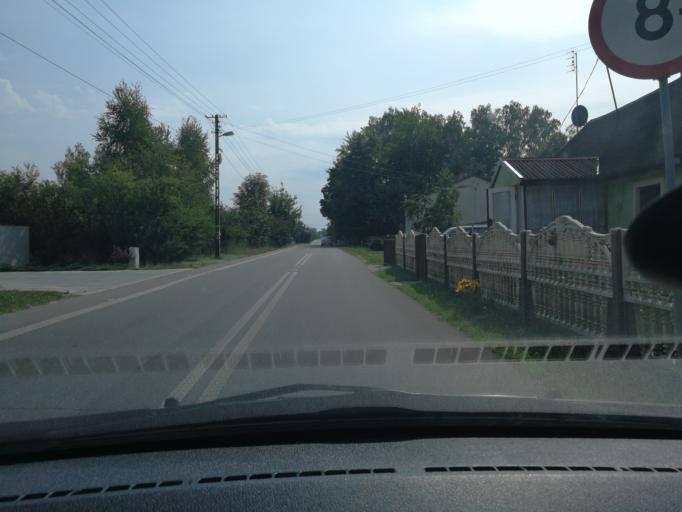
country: PL
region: Lodz Voivodeship
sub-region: powiat Lowicki
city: Bobrowniki
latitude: 52.0194
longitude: 20.0521
